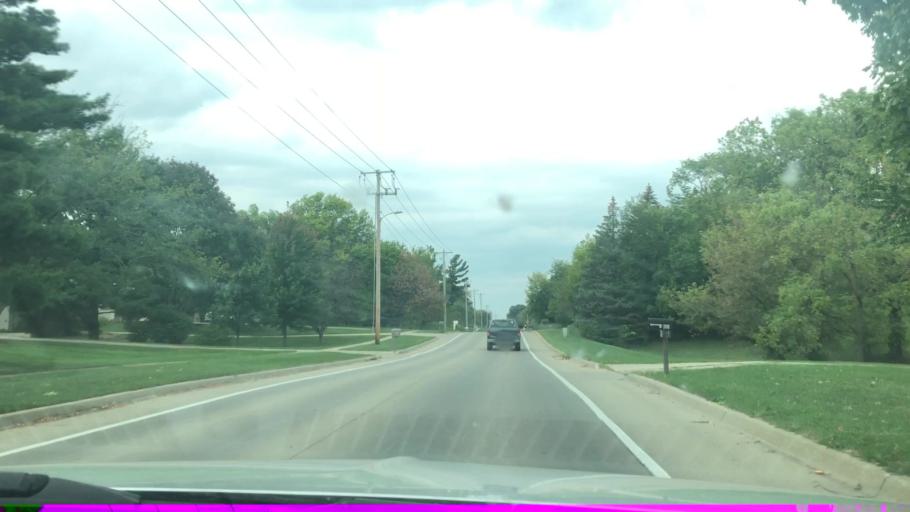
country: US
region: Iowa
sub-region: Marshall County
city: Marshalltown
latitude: 42.0211
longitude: -92.9231
